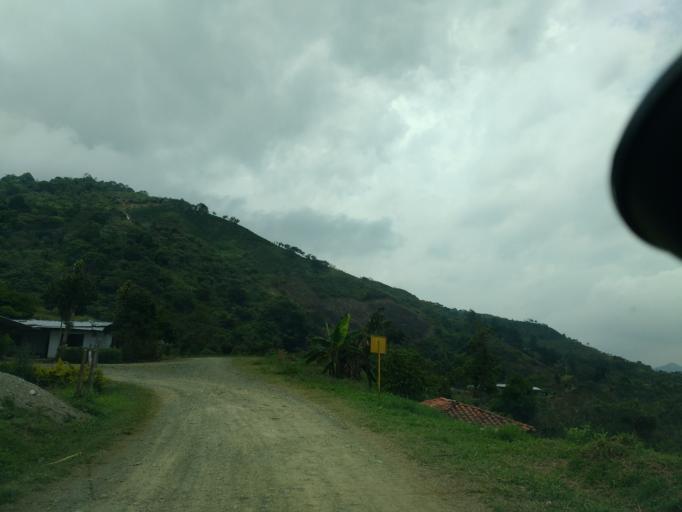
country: CO
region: Cauca
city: Santander de Quilichao
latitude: 2.9180
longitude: -76.4689
